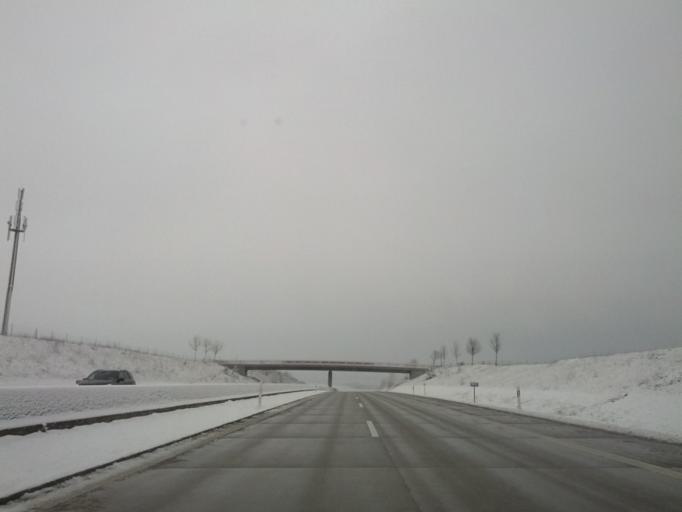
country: DE
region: Bavaria
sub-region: Regierungsbezirk Unterfranken
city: Hollstadt
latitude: 50.3703
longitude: 10.3154
